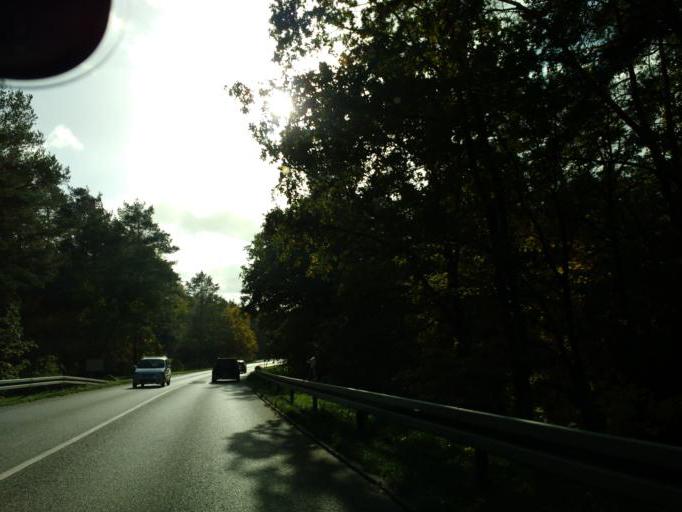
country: DE
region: Brandenburg
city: Petershagen
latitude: 52.5297
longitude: 13.8191
